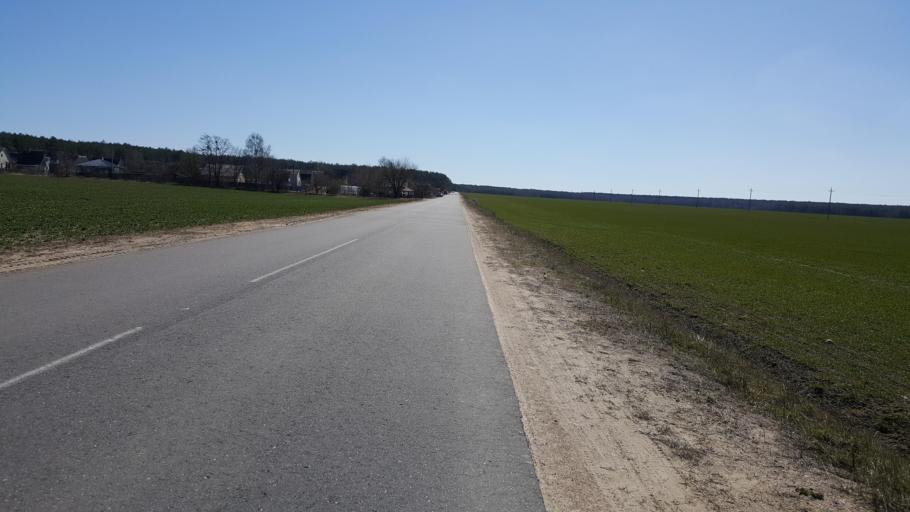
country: BY
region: Brest
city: Kamyanyets
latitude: 52.3694
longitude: 23.7987
